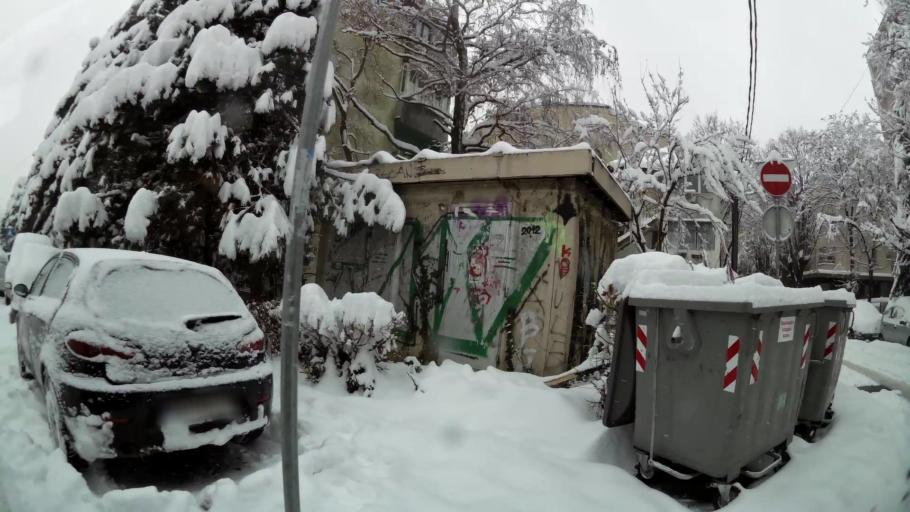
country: RS
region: Central Serbia
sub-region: Belgrade
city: Vracar
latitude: 44.7877
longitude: 20.4850
